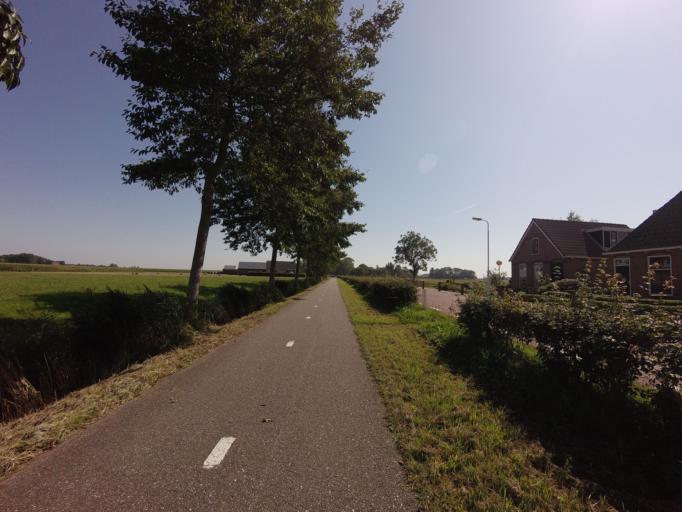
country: NL
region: Friesland
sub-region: Gemeente Dongeradeel
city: Ternaard
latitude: 53.3634
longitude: 5.9739
